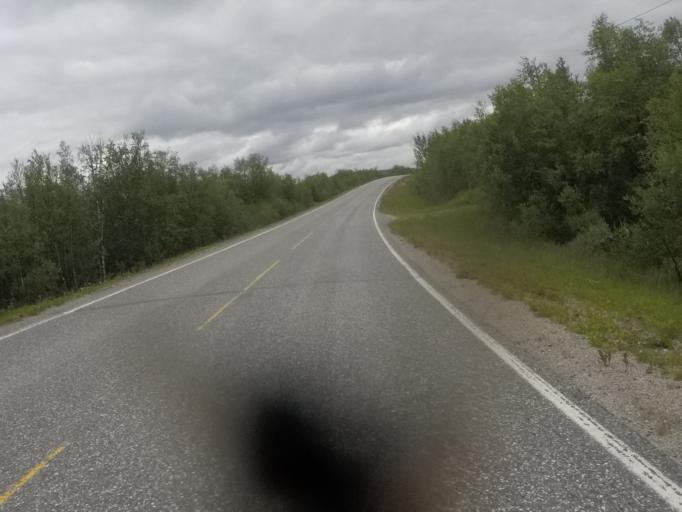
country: NO
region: Finnmark Fylke
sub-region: Kautokeino
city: Kautokeino
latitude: 68.9506
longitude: 23.0882
